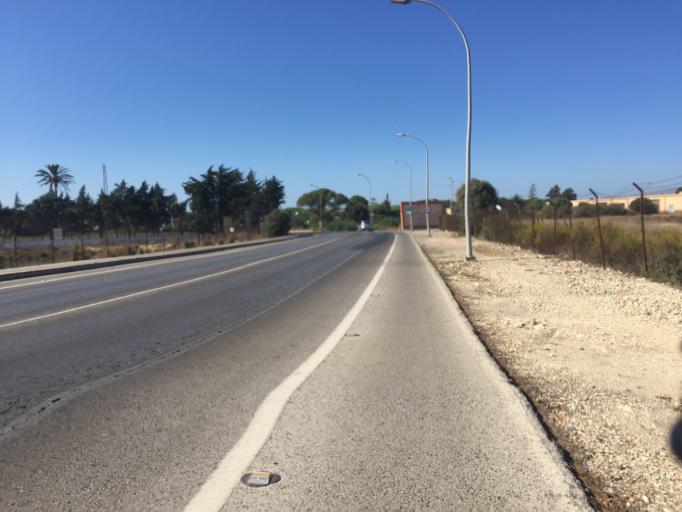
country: ES
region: Andalusia
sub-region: Provincia de Cadiz
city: Chiclana de la Frontera
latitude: 36.3851
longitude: -6.1883
